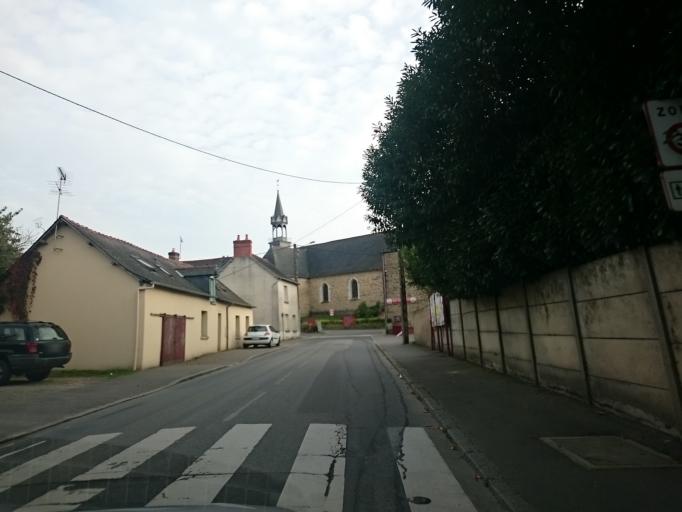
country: FR
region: Brittany
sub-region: Departement d'Ille-et-Vilaine
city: Bourgbarre
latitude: 47.9959
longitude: -1.6156
